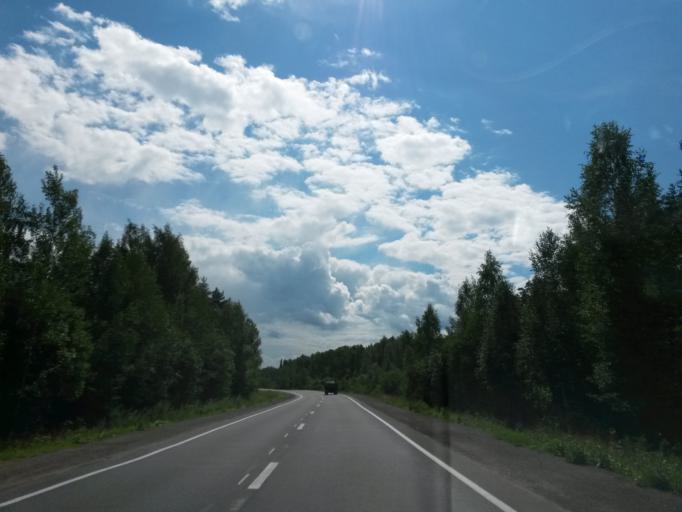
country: RU
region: Jaroslavl
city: Gavrilov-Yam
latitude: 57.2939
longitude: 39.9497
